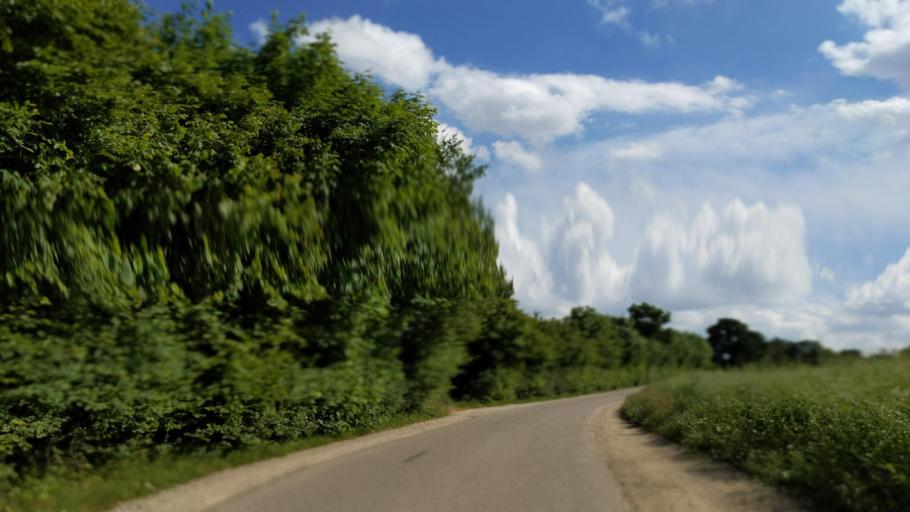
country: DE
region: Schleswig-Holstein
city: Timmendorfer Strand
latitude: 53.9921
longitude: 10.7537
